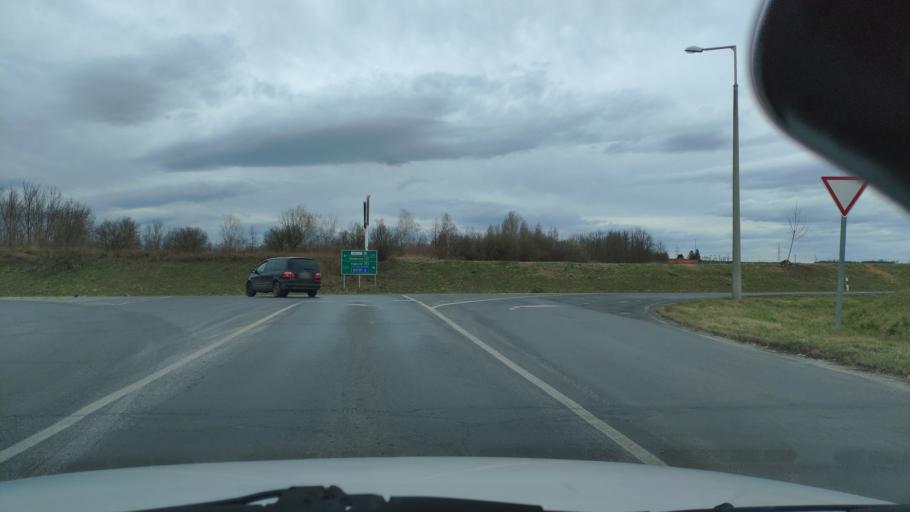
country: HU
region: Zala
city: Nagykanizsa
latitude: 46.4653
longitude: 17.0079
